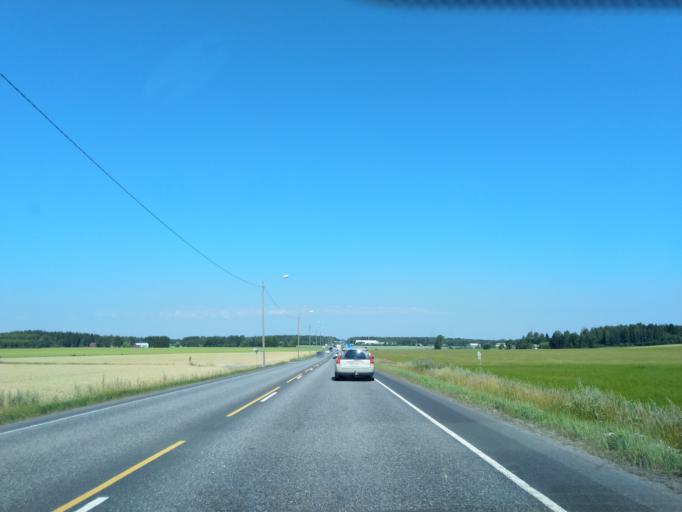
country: FI
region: Satakunta
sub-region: Pori
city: Nakkila
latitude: 61.3701
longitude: 21.9808
